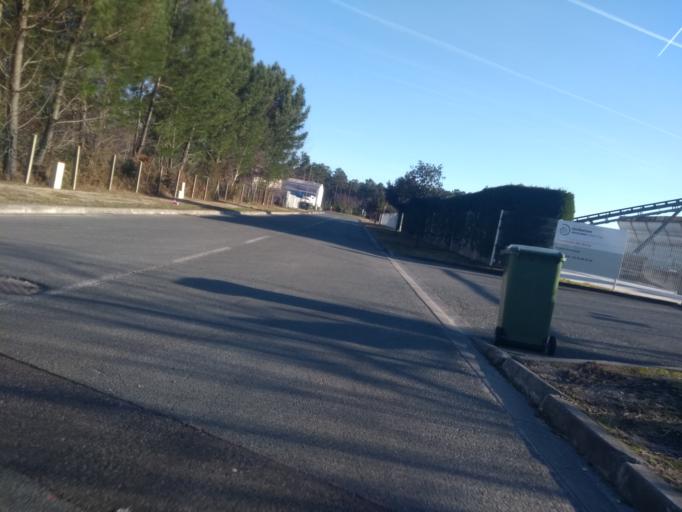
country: FR
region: Aquitaine
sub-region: Departement de la Gironde
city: Le Barp
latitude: 44.6208
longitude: -0.7870
